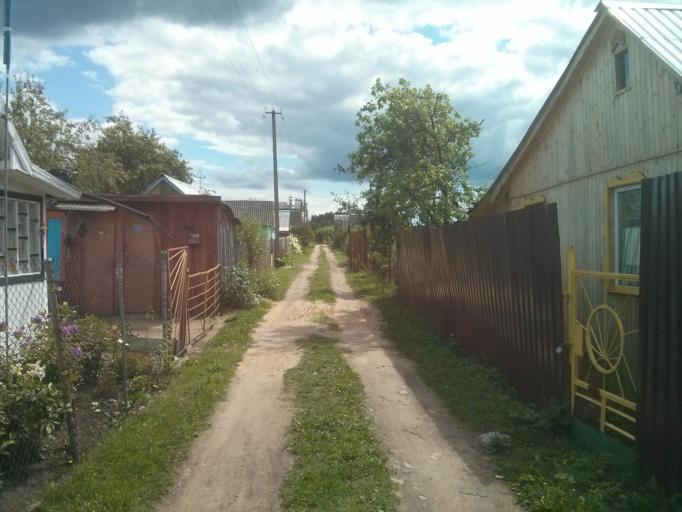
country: BY
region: Vitebsk
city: Navapolatsk
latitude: 55.5353
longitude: 28.5945
